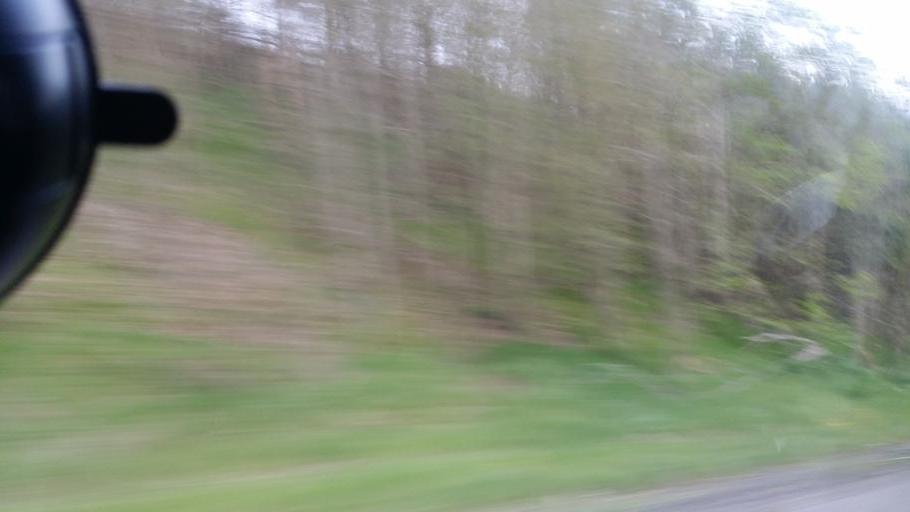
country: IE
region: Ulster
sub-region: An Cabhan
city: Cavan
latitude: 53.9873
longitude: -7.3385
